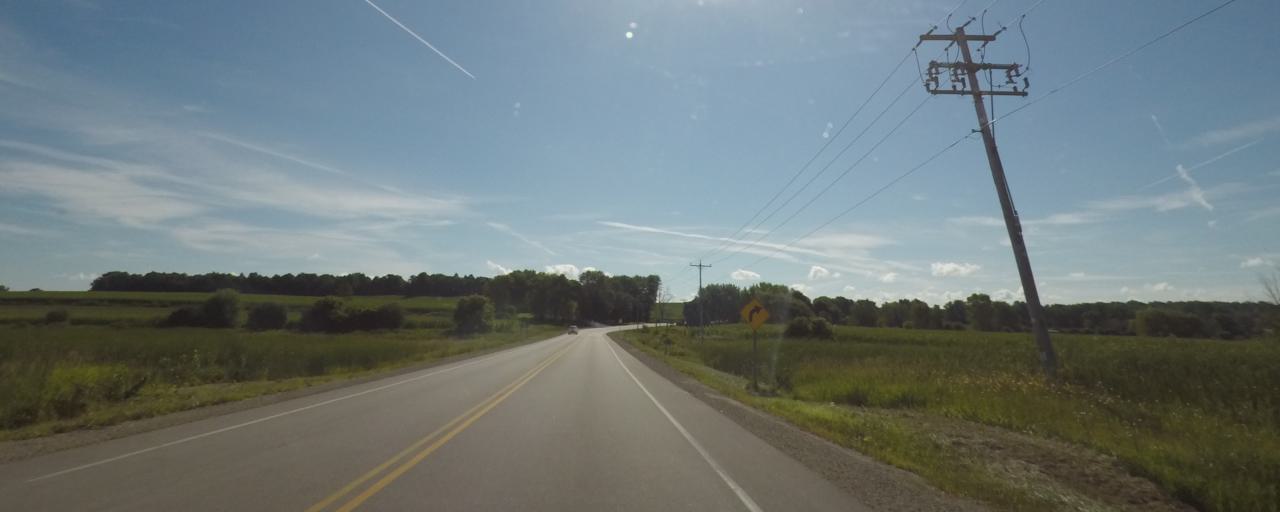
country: US
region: Wisconsin
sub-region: Jefferson County
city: Johnson Creek
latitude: 43.0754
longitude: -88.7170
